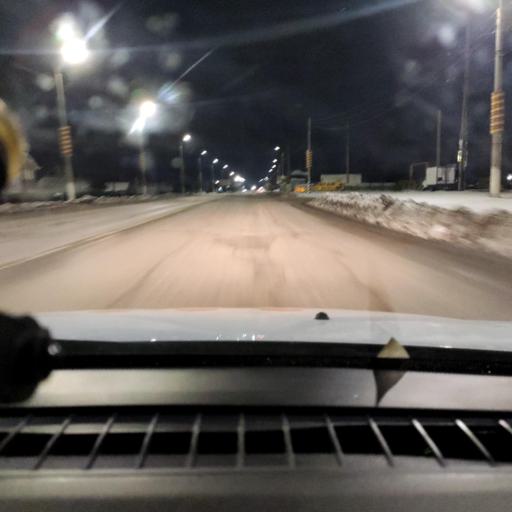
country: RU
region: Samara
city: Novokuybyshevsk
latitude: 53.0837
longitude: 49.9577
